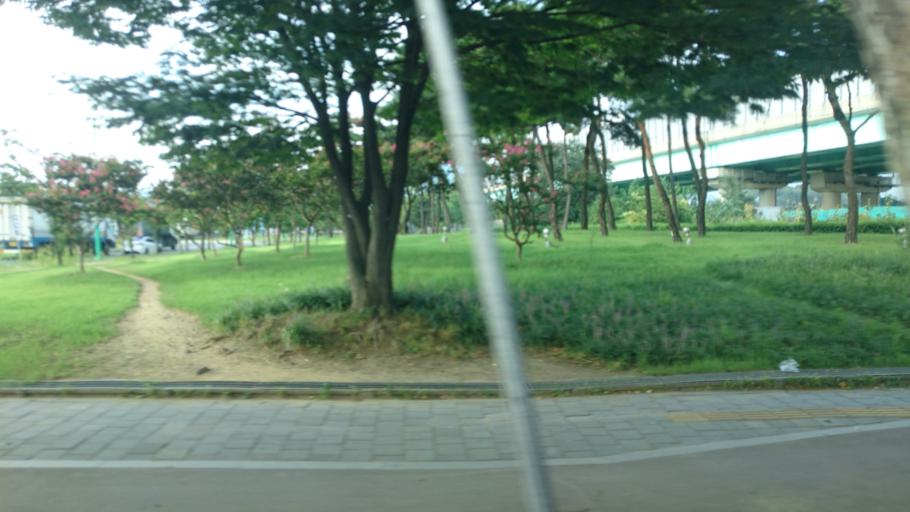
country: KR
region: Gyeongsangbuk-do
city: Gyeongsan-si
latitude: 35.8754
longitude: 128.6847
